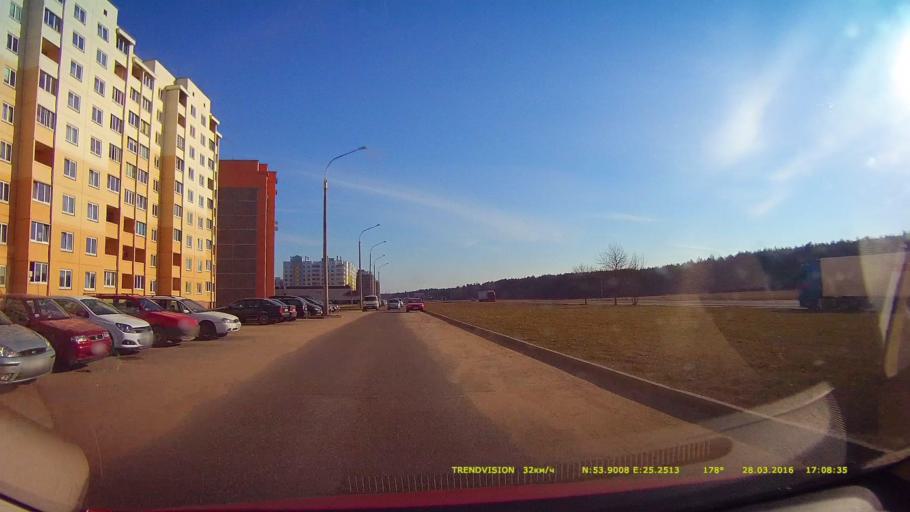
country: BY
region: Grodnenskaya
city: Lida
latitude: 53.9005
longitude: 25.2513
